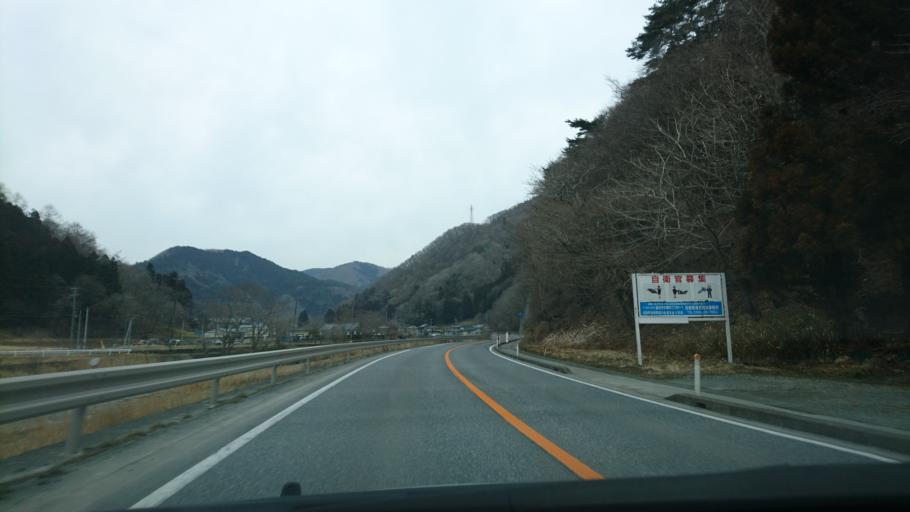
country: JP
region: Iwate
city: Tono
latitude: 39.1457
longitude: 141.5473
